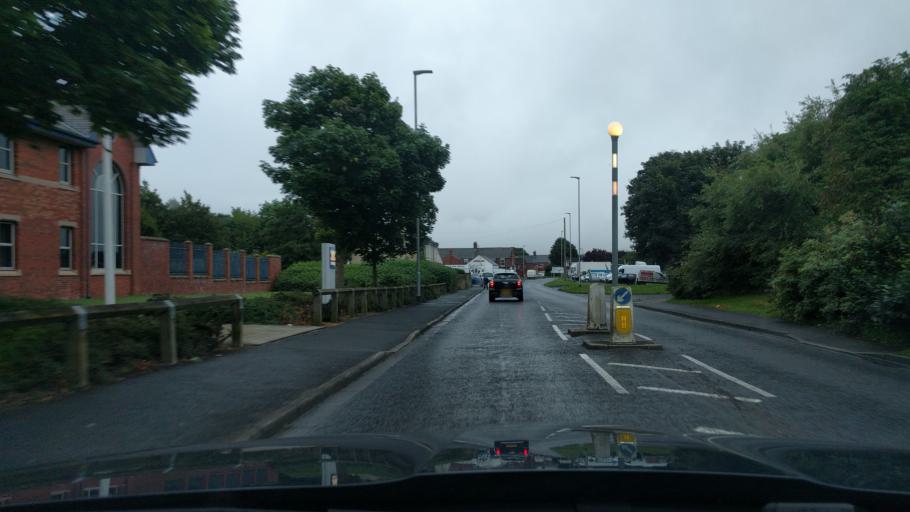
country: GB
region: England
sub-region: Northumberland
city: Bedlington
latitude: 55.1328
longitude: -1.5936
